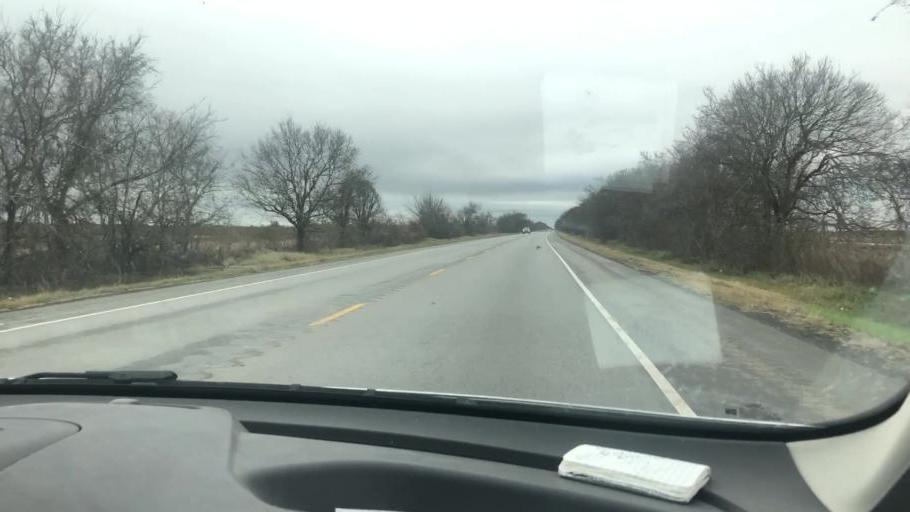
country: US
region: Texas
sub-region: Matagorda County
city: Van Vleck
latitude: 29.1197
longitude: -95.9808
